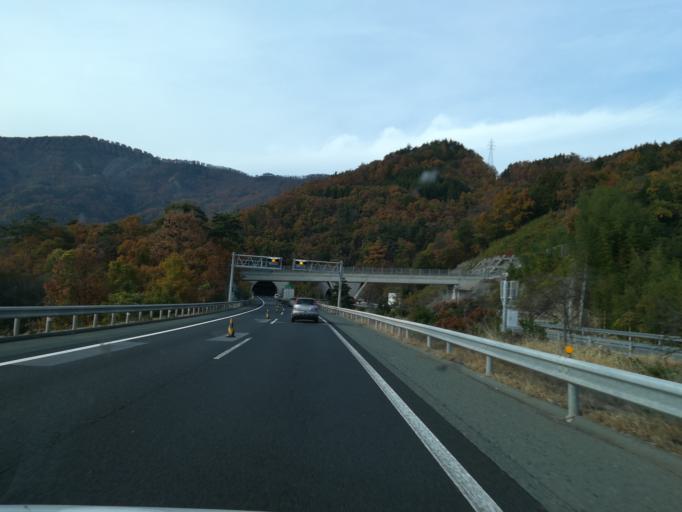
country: JP
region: Nagano
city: Ueda
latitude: 36.4725
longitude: 138.1970
